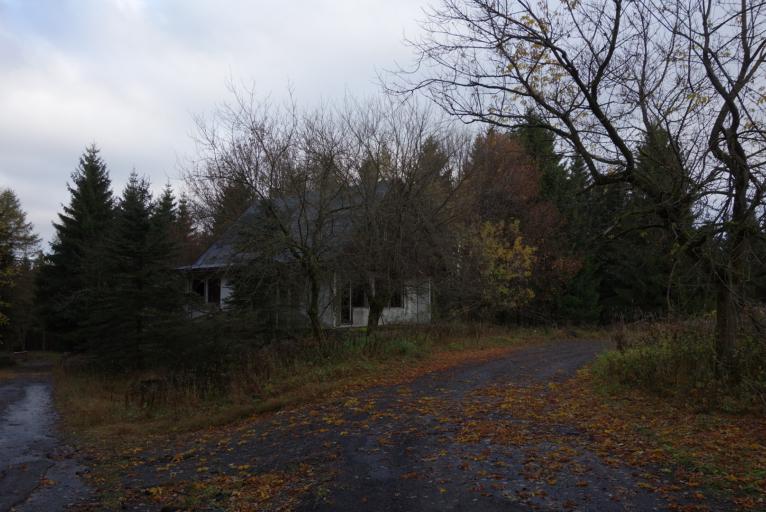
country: DE
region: Saxony
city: Pobershau
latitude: 50.5814
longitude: 13.2535
